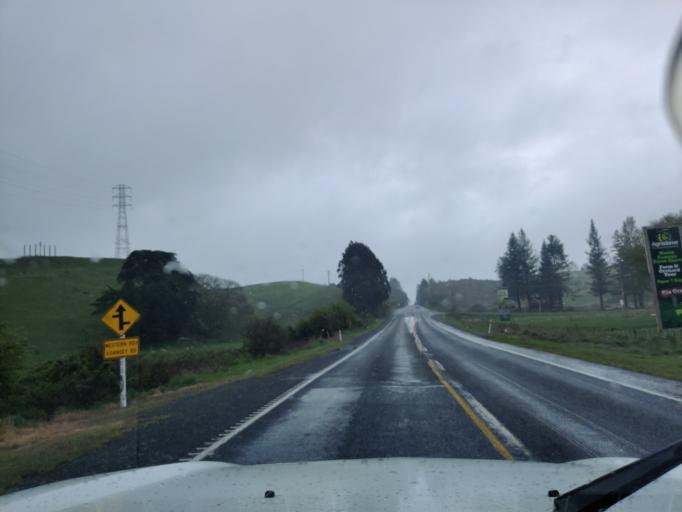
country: NZ
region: Bay of Plenty
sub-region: Rotorua District
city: Rotorua
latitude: -38.0848
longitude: 176.1892
